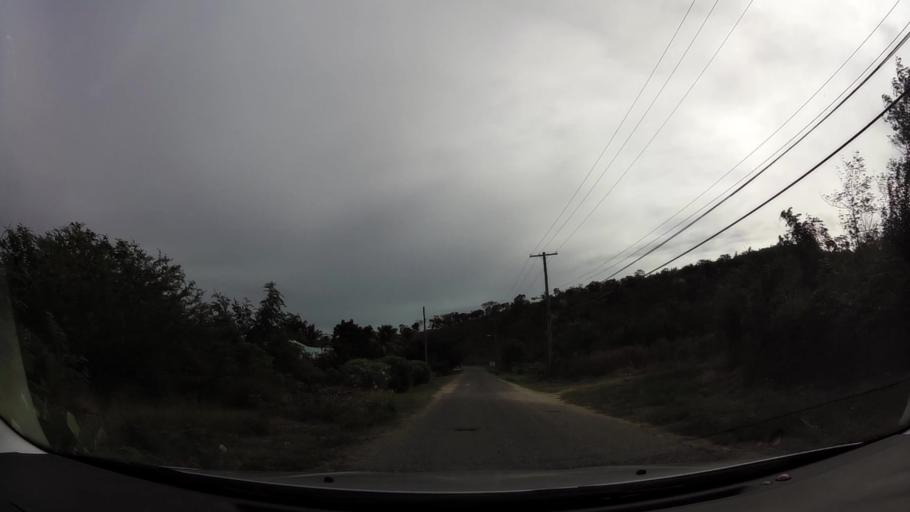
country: AG
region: Saint Peter
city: Parham
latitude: 17.0635
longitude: -61.7287
